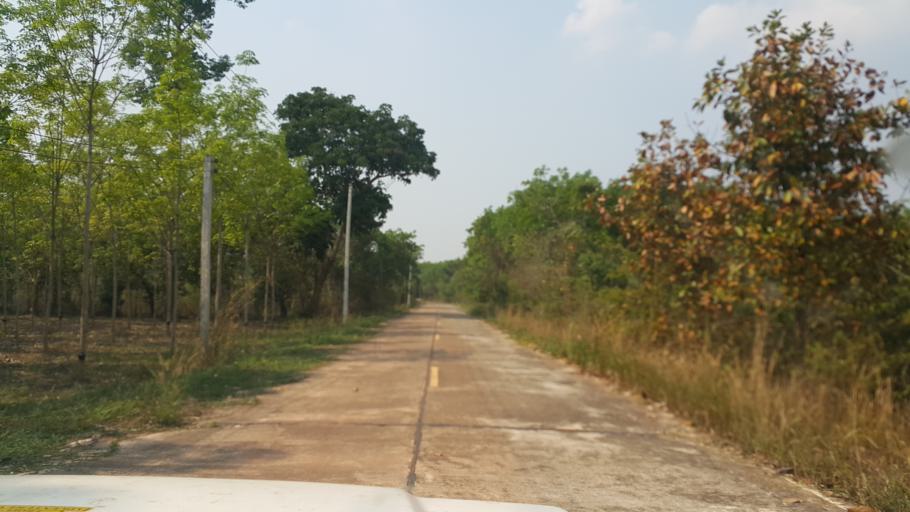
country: TH
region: Nakhon Phanom
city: Ban Phaeng
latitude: 17.9682
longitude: 104.1538
